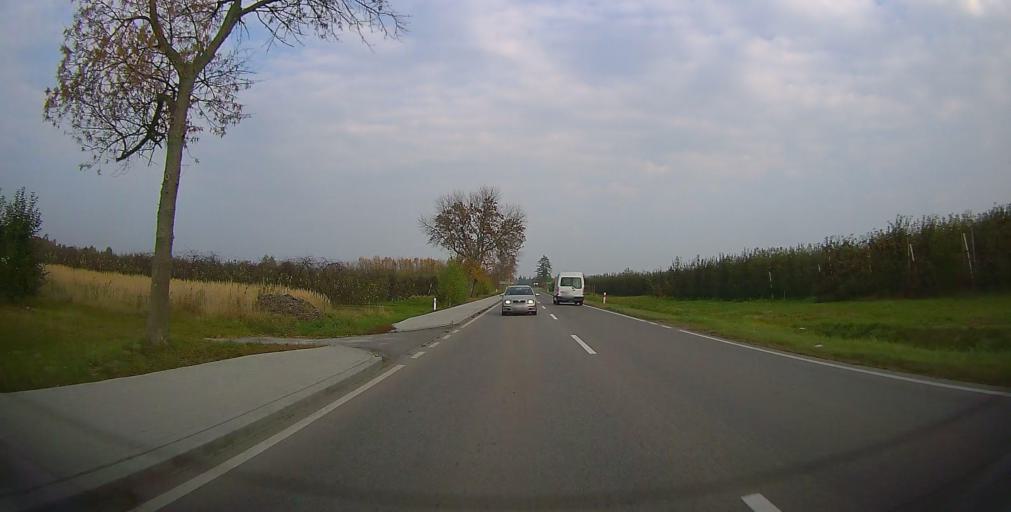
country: PL
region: Masovian Voivodeship
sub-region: Powiat grojecki
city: Belsk Duzy
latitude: 51.7689
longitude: 20.7685
